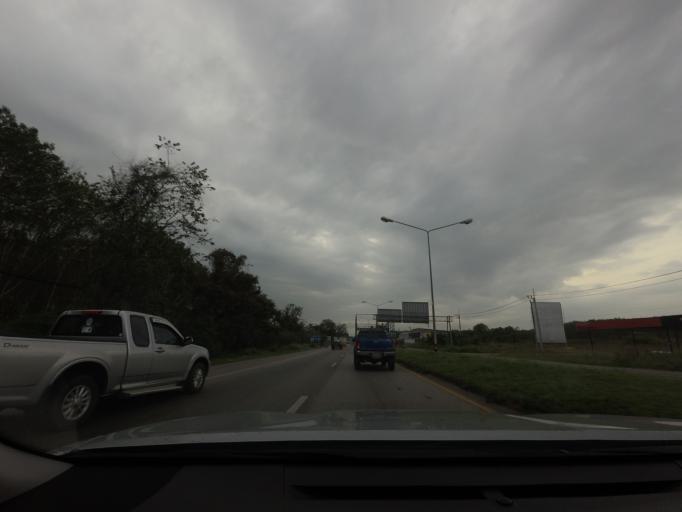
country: TH
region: Surat Thani
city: Phunphin
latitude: 9.0483
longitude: 99.1605
